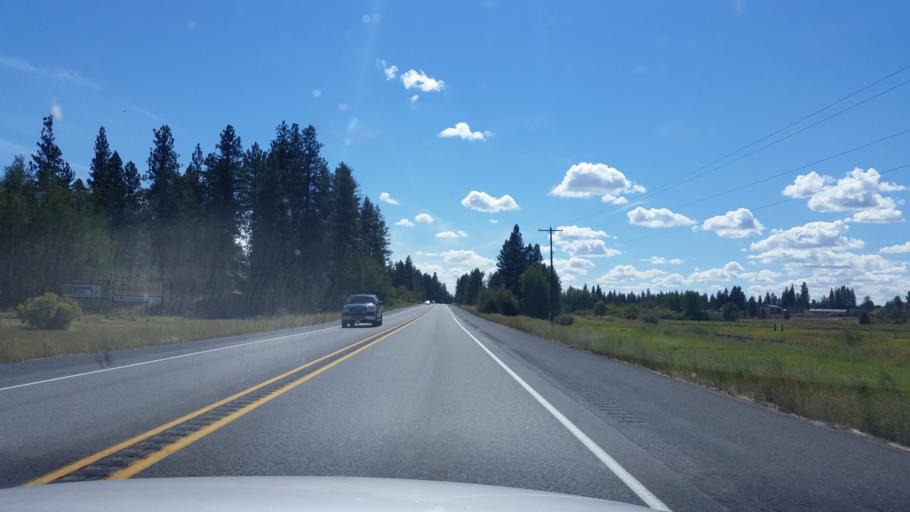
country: US
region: Washington
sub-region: Spokane County
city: Cheney
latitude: 47.5244
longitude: -117.5662
